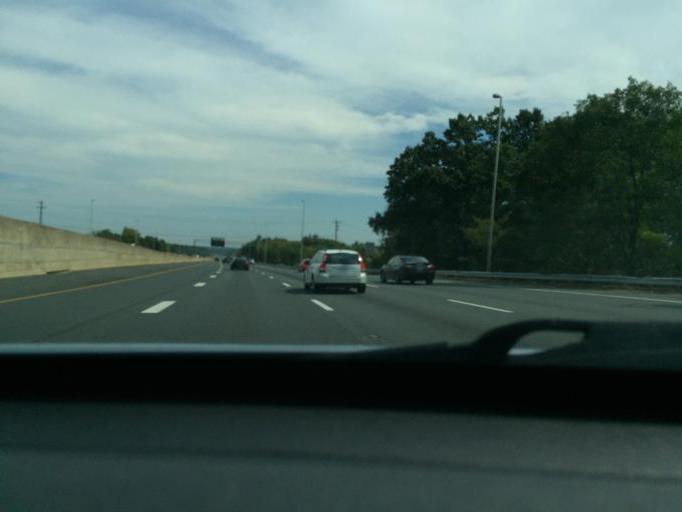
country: US
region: Virginia
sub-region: Prince William County
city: Sudley
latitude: 38.8026
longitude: -77.5089
